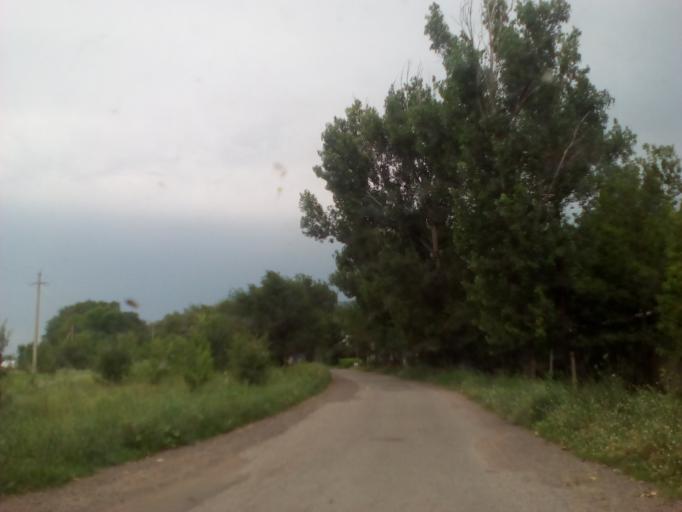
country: KZ
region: Almaty Oblysy
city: Burunday
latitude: 43.1598
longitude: 76.3882
